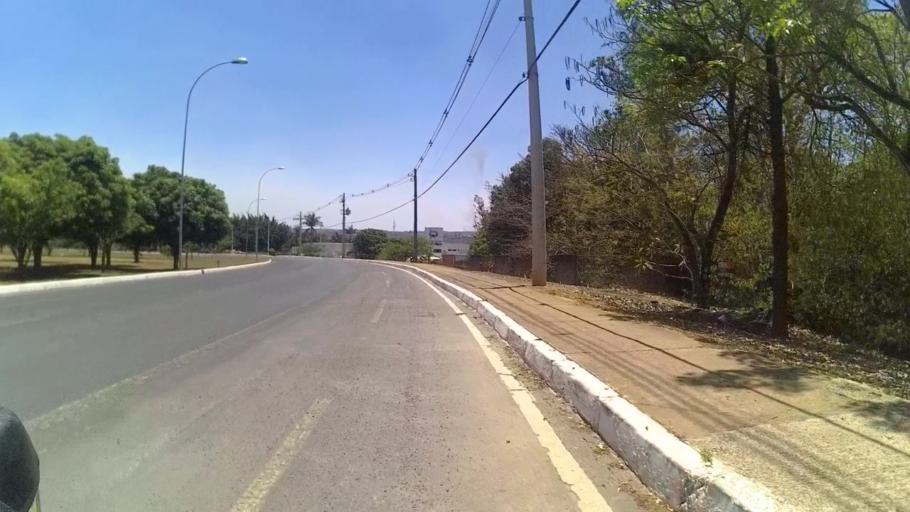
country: BR
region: Federal District
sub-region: Brasilia
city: Brasilia
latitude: -15.7613
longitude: -47.8319
